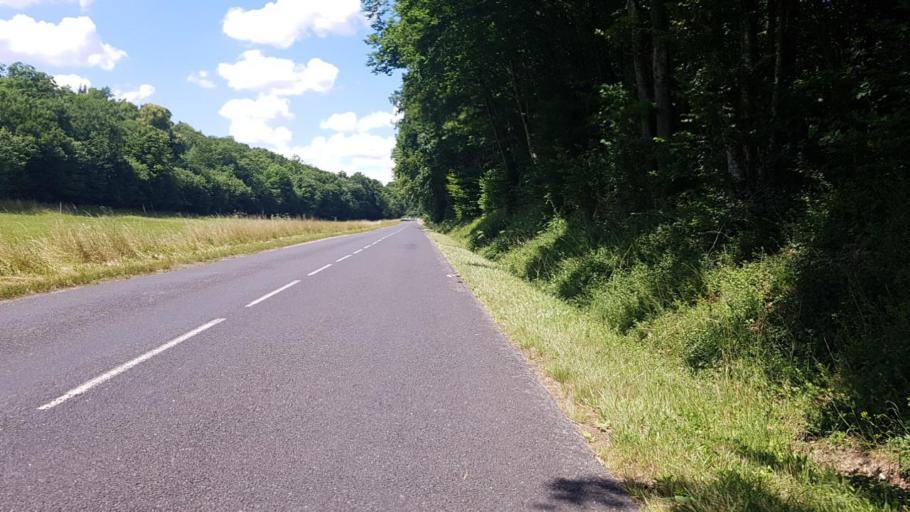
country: FR
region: Lorraine
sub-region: Departement de la Meuse
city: Vacon
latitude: 48.6710
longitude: 5.5647
